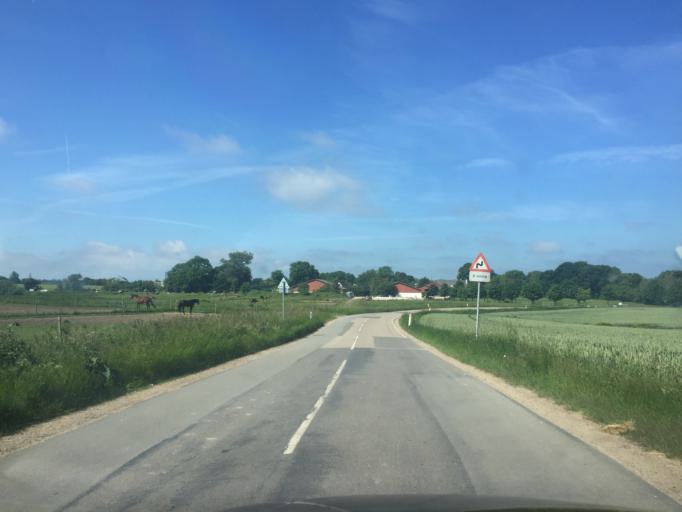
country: DK
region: Capital Region
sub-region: Hoje-Taastrup Kommune
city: Flong
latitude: 55.6778
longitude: 12.1974
